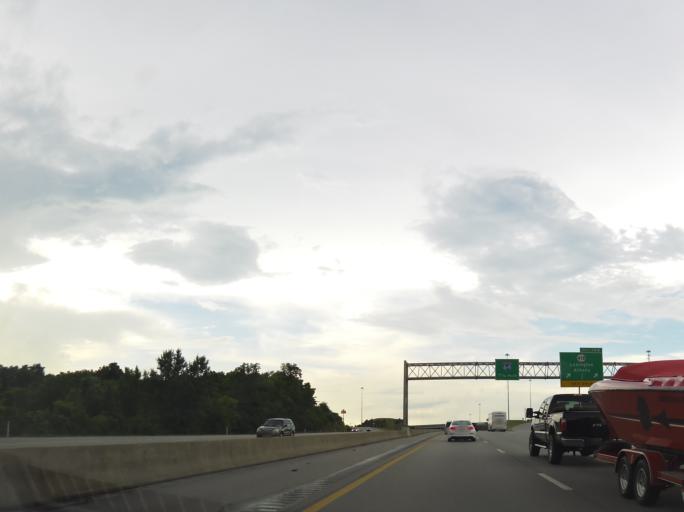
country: US
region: Kentucky
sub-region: Fayette County
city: Lexington
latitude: 37.9585
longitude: -84.3887
